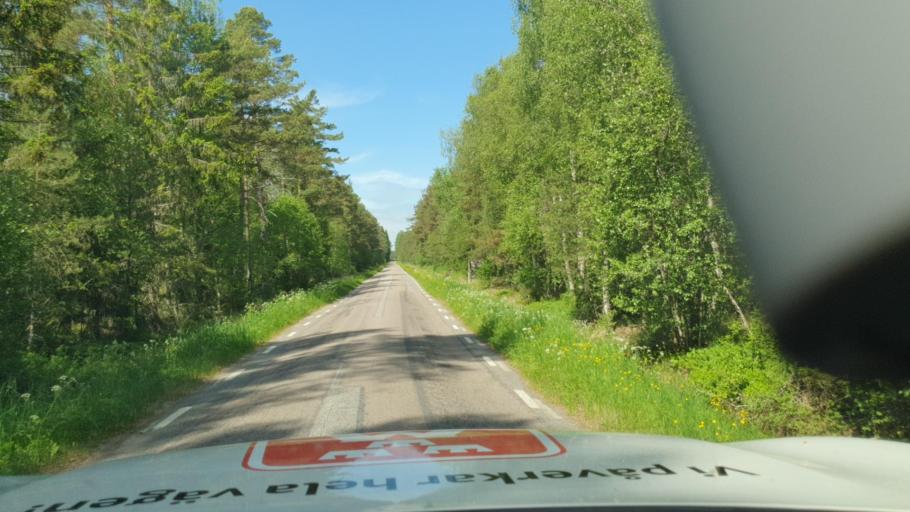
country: SE
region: Vaestra Goetaland
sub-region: Herrljunga Kommun
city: Herrljunga
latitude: 58.1198
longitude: 13.1037
